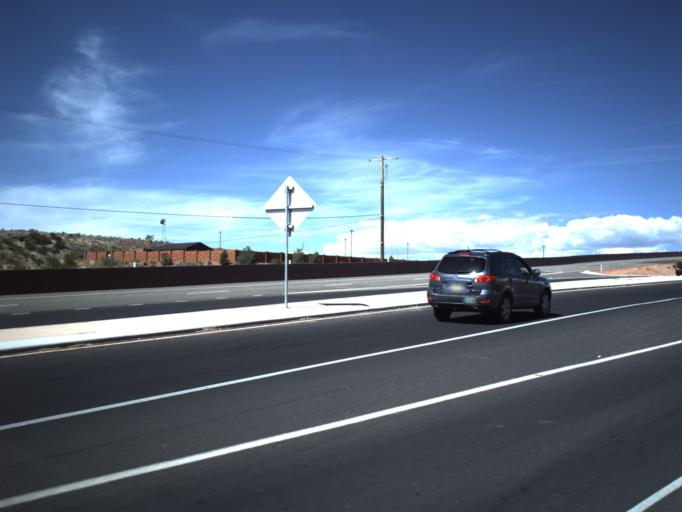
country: US
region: Utah
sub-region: Washington County
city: Saint George
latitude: 37.1315
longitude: -113.6028
